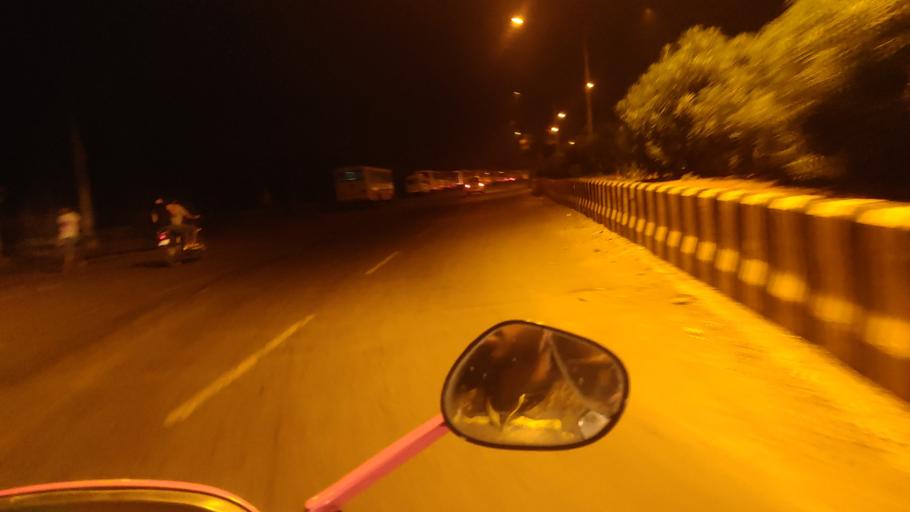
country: IN
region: Maharashtra
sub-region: Thane
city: Bhayandar
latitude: 19.2944
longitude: 72.8420
